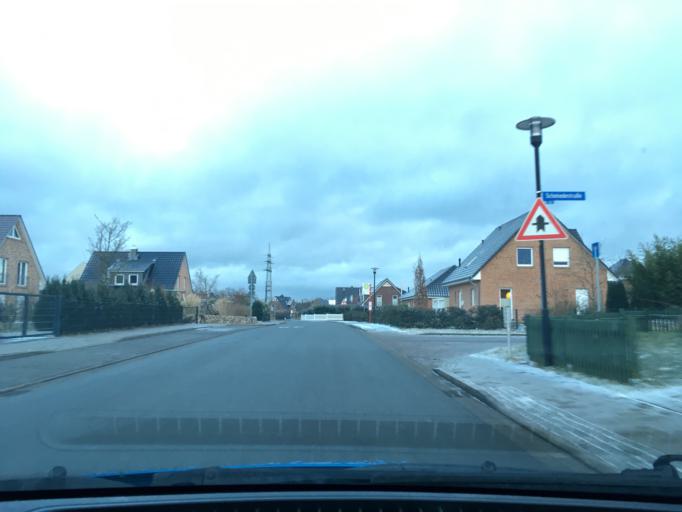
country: DE
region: Lower Saxony
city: Reppenstedt
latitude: 53.2249
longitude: 10.3761
